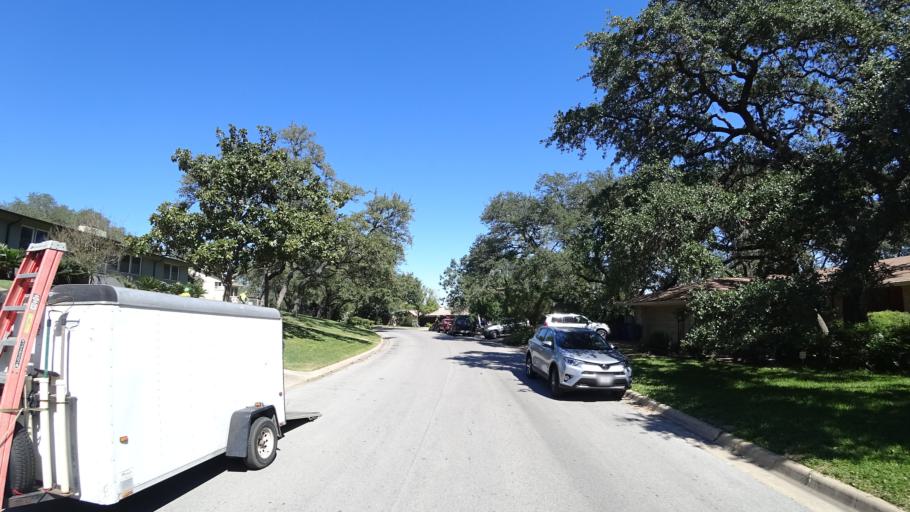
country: US
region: Texas
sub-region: Travis County
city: West Lake Hills
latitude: 30.3371
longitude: -97.7603
